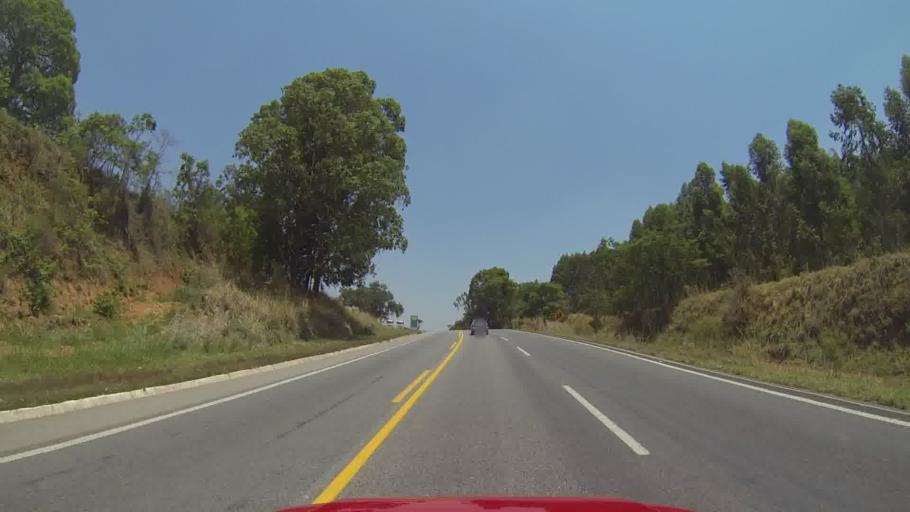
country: BR
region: Minas Gerais
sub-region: Itapecerica
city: Itapecerica
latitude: -20.2790
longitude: -45.1289
